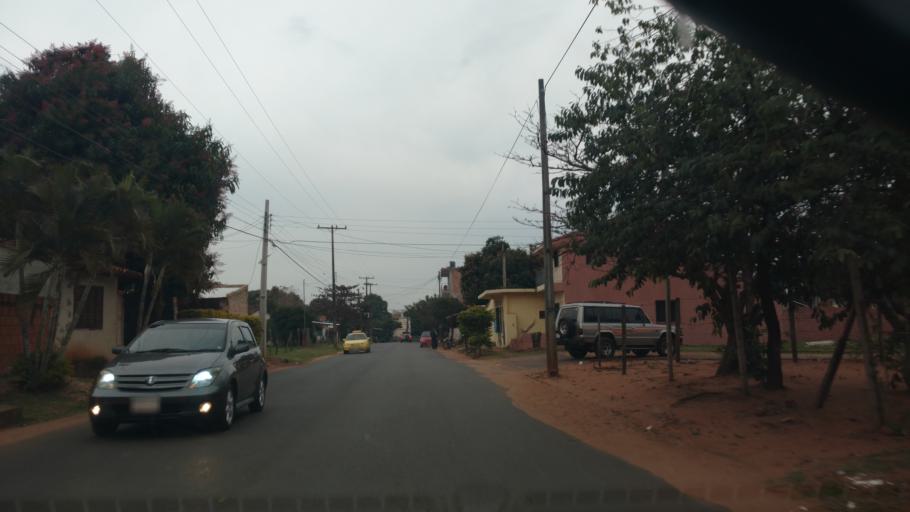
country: PY
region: Central
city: Capiata
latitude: -25.3594
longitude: -57.4710
